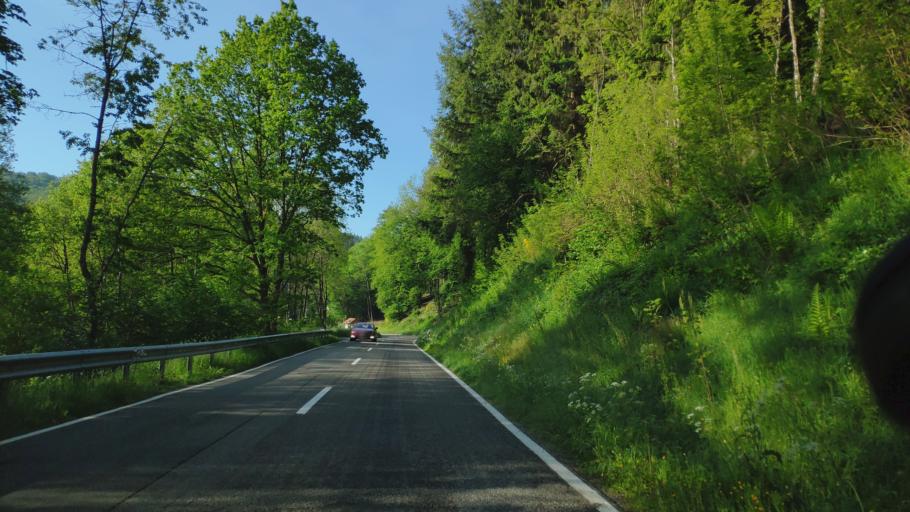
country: DE
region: Rheinland-Pfalz
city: Ruppertsweiler
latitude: 49.1704
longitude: 7.7177
